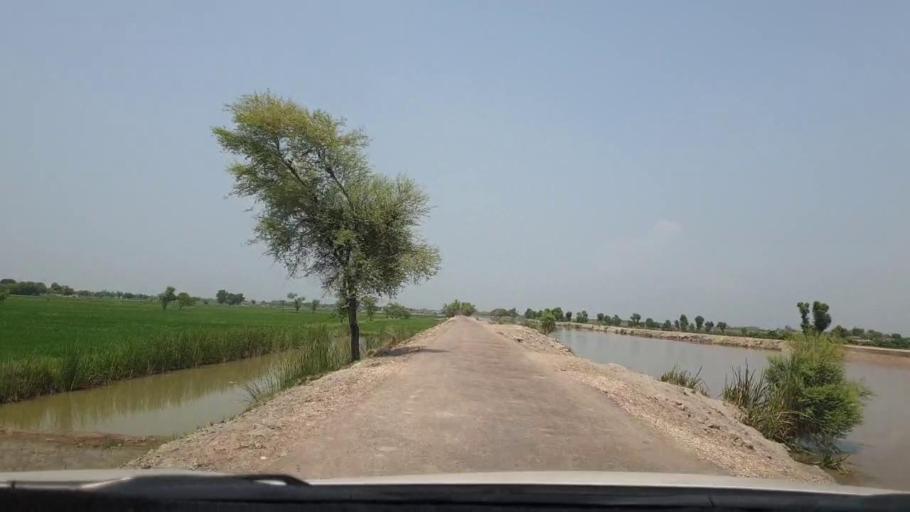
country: PK
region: Sindh
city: Dokri
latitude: 27.3394
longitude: 68.1107
